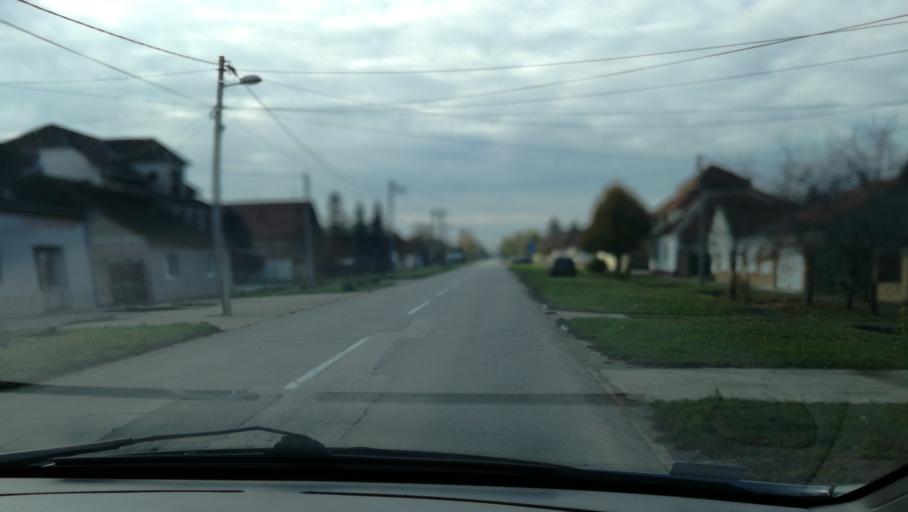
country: RS
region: Autonomna Pokrajina Vojvodina
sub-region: Severnobanatski Okrug
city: Kikinda
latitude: 45.8300
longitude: 20.4401
